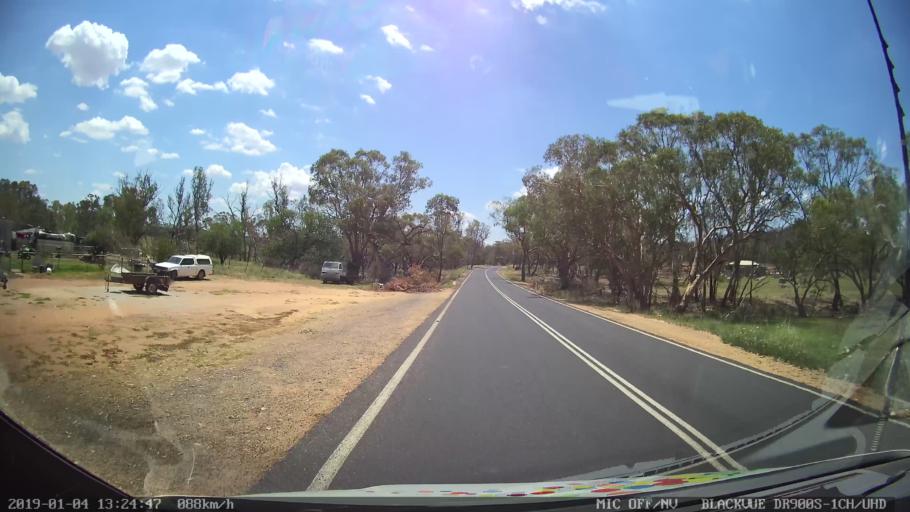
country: AU
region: New South Wales
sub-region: Parkes
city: Peak Hill
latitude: -32.7011
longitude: 148.5535
